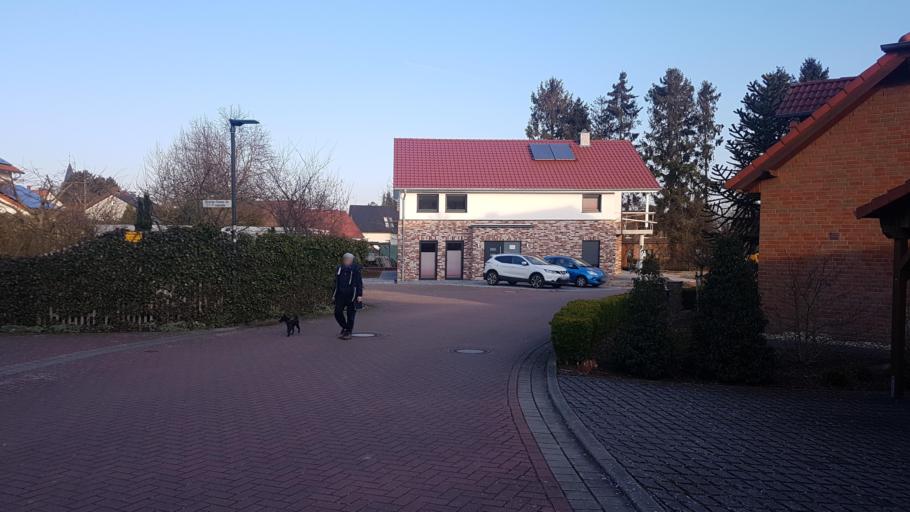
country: DE
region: Lower Saxony
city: Springe
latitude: 52.2153
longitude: 9.6198
